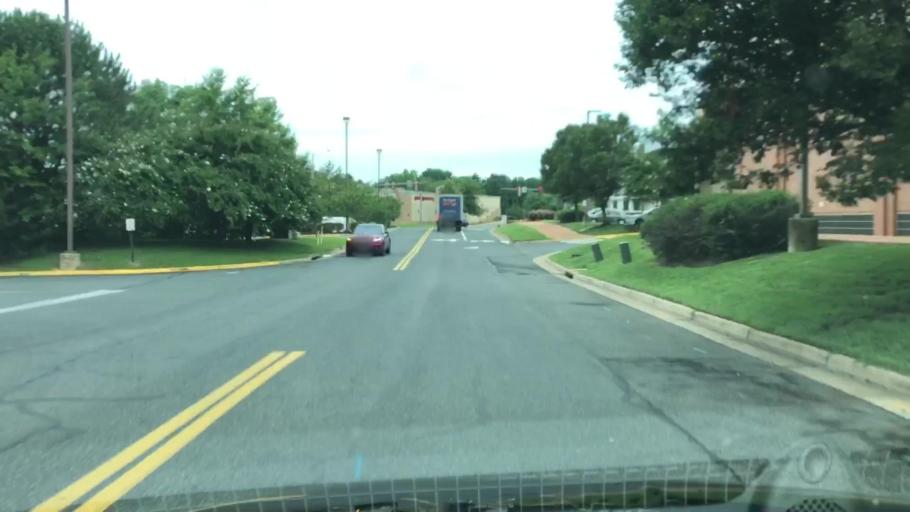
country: US
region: Virginia
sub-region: Stafford County
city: Falmouth
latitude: 38.3006
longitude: -77.5127
